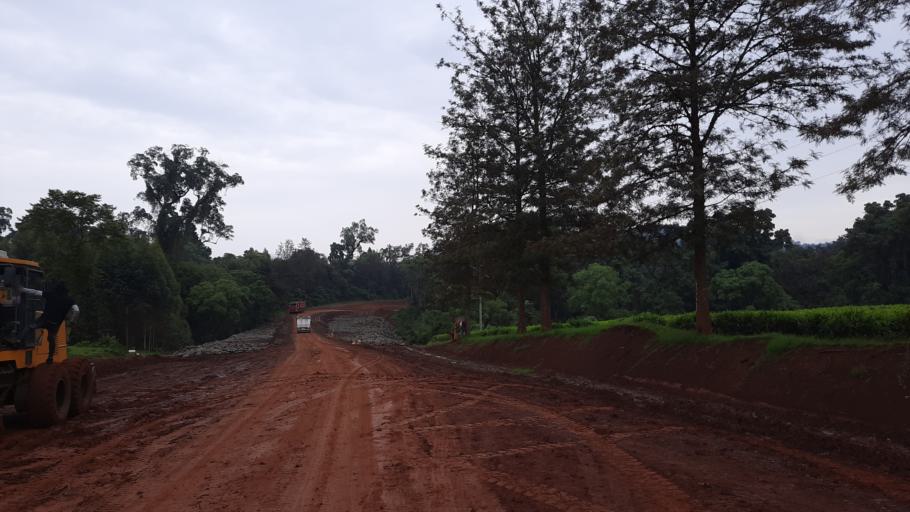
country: ET
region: Oromiya
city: Gore
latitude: 7.8618
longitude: 35.4775
